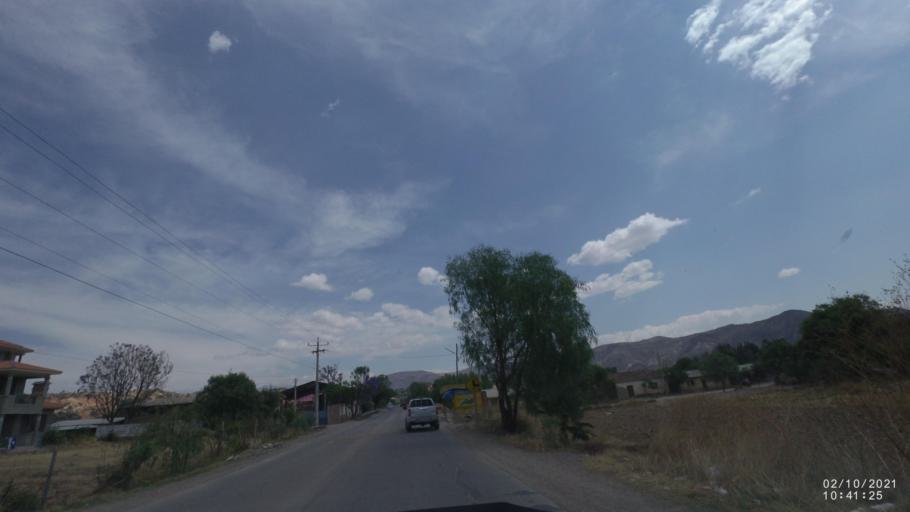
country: BO
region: Cochabamba
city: Capinota
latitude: -17.6141
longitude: -66.2908
